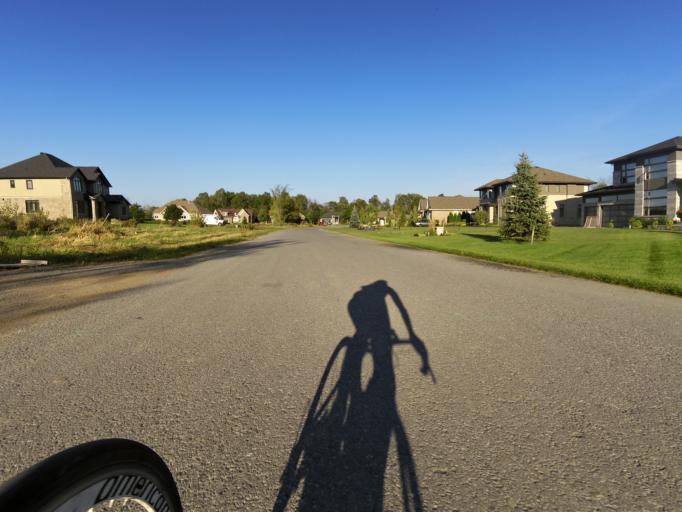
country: CA
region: Ontario
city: Bells Corners
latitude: 45.2149
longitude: -75.7057
